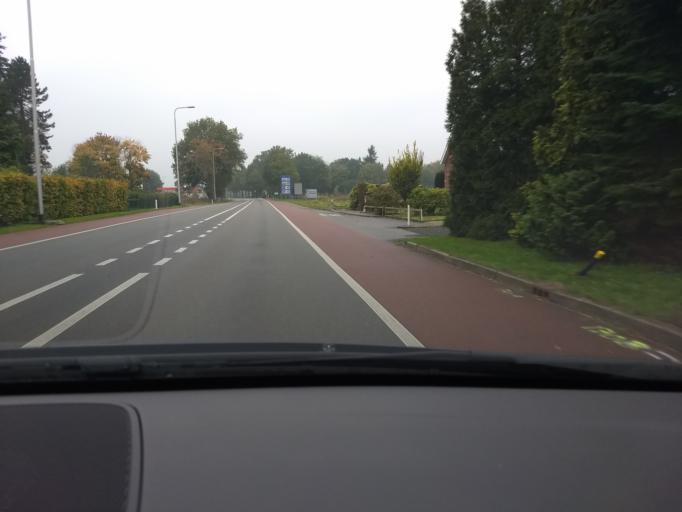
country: DE
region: North Rhine-Westphalia
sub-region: Regierungsbezirk Munster
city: Sudlohn
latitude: 51.9372
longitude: 6.7942
